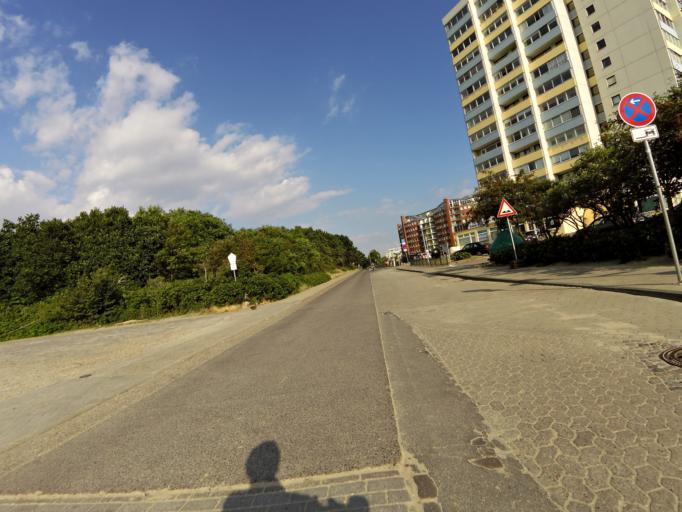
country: DE
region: Lower Saxony
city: Nordholz
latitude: 53.8630
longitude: 8.5964
